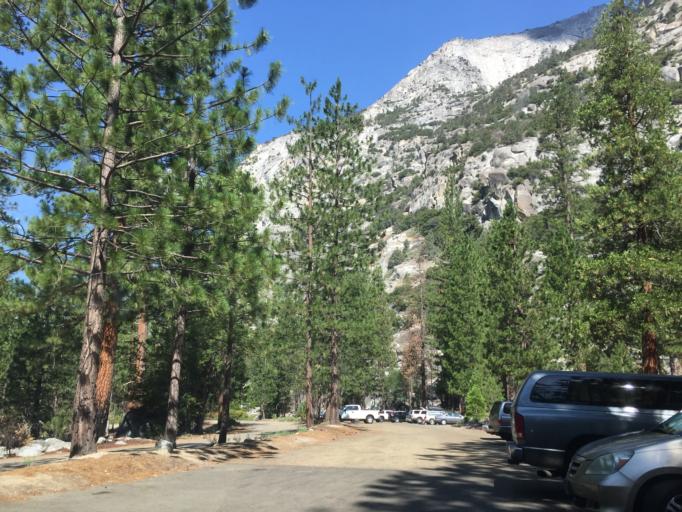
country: US
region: California
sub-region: Inyo County
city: Big Pine
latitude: 36.7962
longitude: -118.5831
